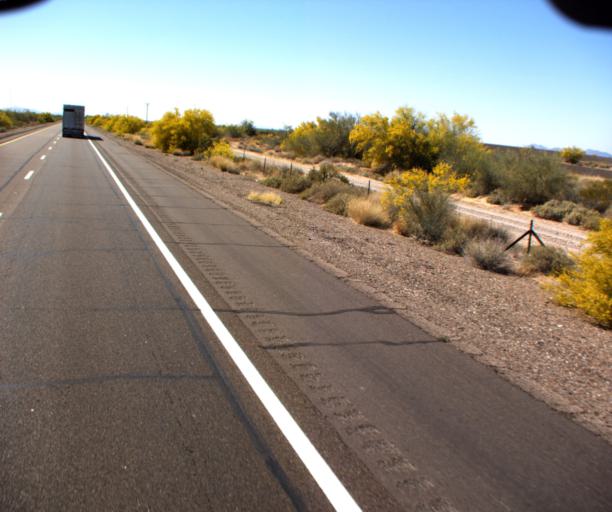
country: US
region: Arizona
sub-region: Maricopa County
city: Gila Bend
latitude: 32.8373
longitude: -113.3458
